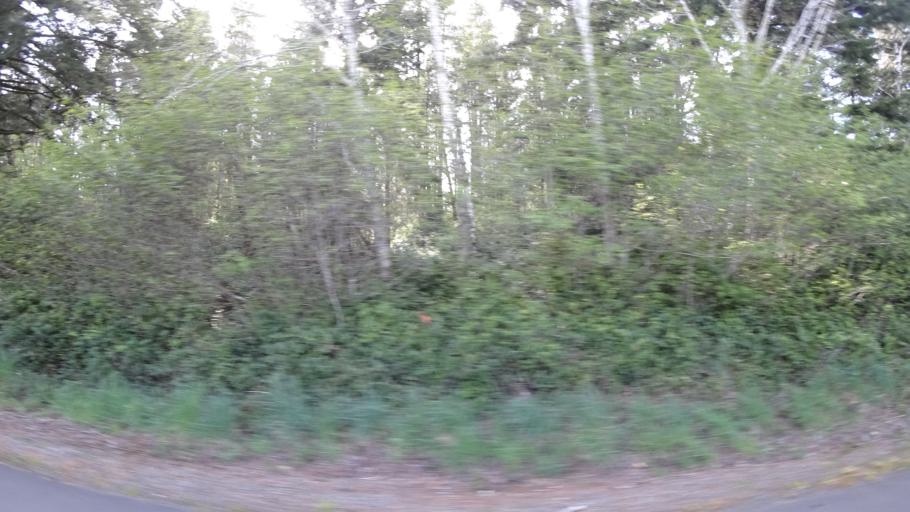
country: US
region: Oregon
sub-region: Lane County
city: Dunes City
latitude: 43.9089
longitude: -124.1122
